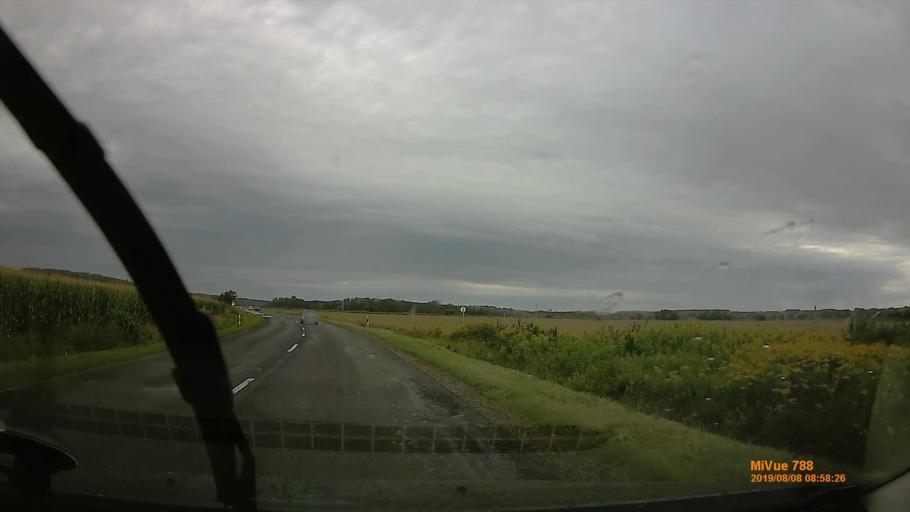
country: HU
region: Zala
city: Pacsa
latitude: 46.6597
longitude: 16.9191
